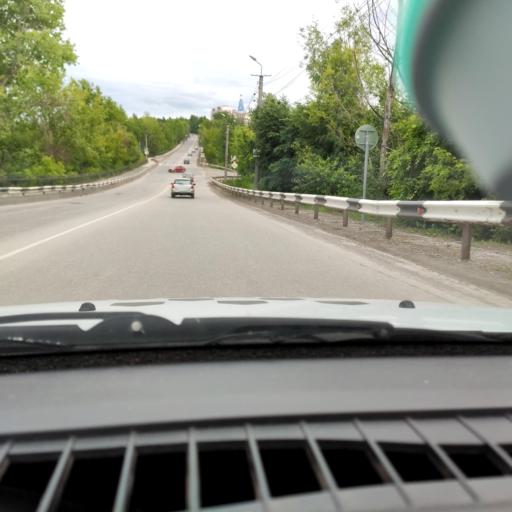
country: RU
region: Perm
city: Chusovoy
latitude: 58.2844
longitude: 57.8128
